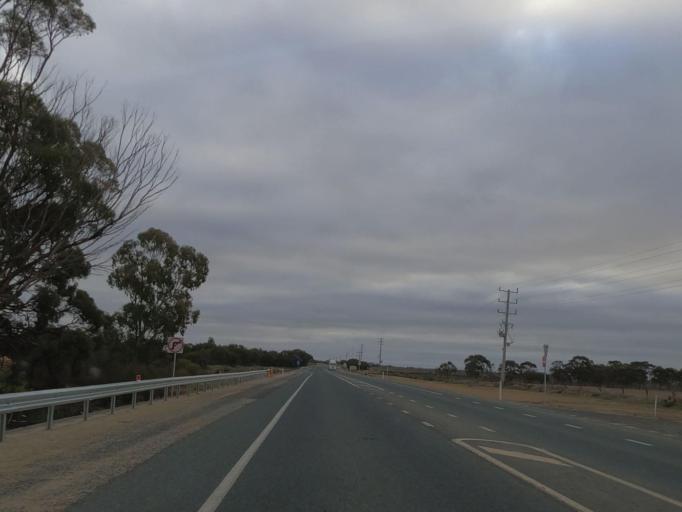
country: AU
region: Victoria
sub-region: Swan Hill
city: Swan Hill
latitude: -35.5468
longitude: 143.7620
